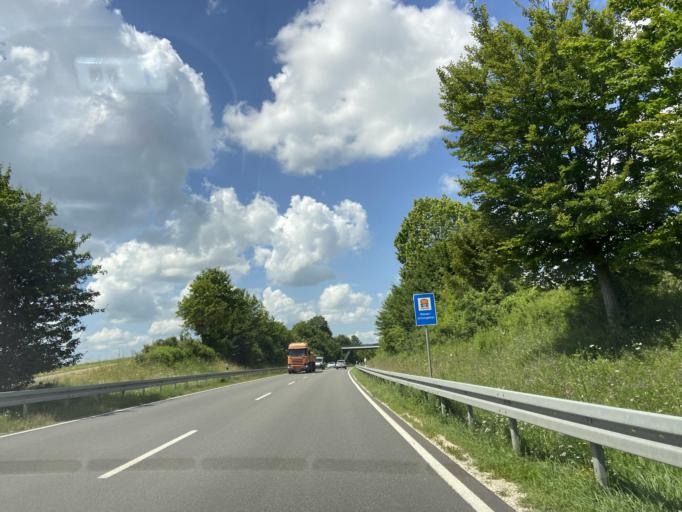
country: DE
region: Baden-Wuerttemberg
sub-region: Tuebingen Region
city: Winterlingen
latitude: 48.1714
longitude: 9.1132
